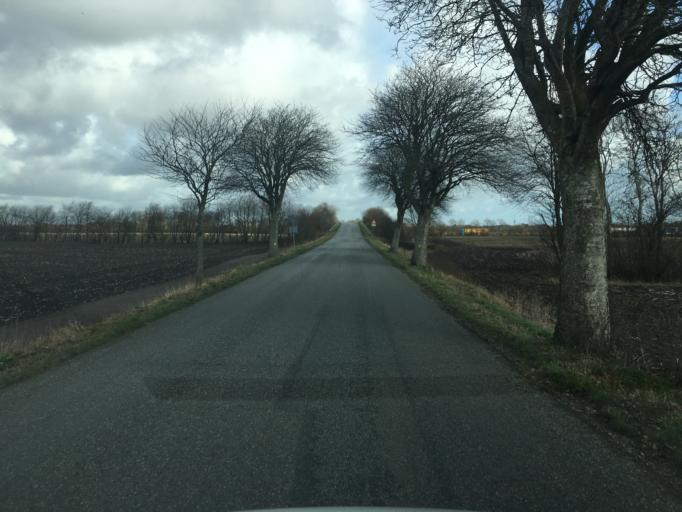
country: DK
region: South Denmark
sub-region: Aabenraa Kommune
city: Krusa
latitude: 54.9015
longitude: 9.3719
